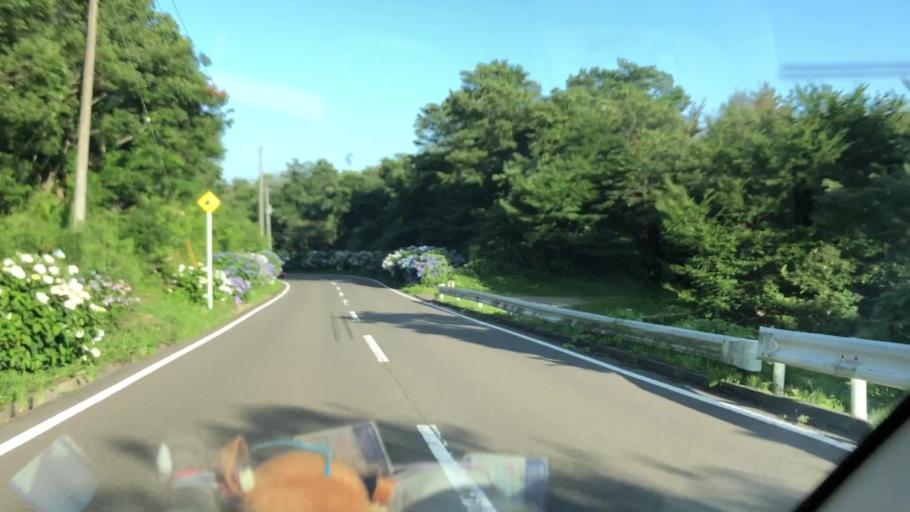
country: JP
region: Miyagi
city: Shiroishi
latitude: 38.0210
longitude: 140.5522
